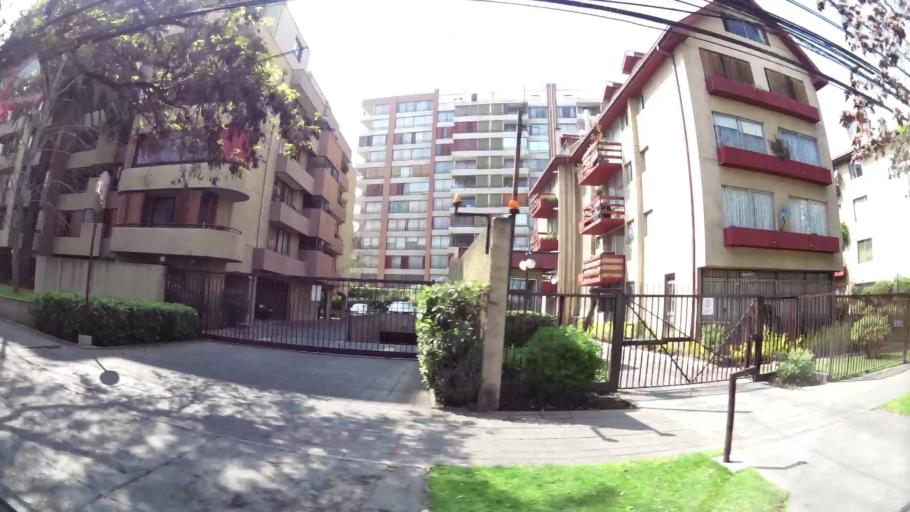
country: CL
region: Santiago Metropolitan
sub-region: Provincia de Santiago
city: Villa Presidente Frei, Nunoa, Santiago, Chile
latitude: -33.4513
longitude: -70.6003
